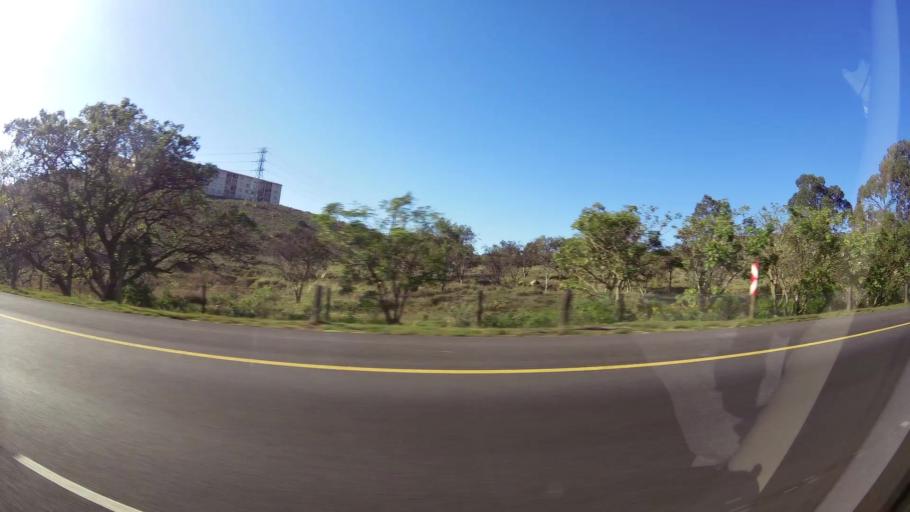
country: ZA
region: Eastern Cape
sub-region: Nelson Mandela Bay Metropolitan Municipality
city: Port Elizabeth
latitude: -33.9351
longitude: 25.5568
